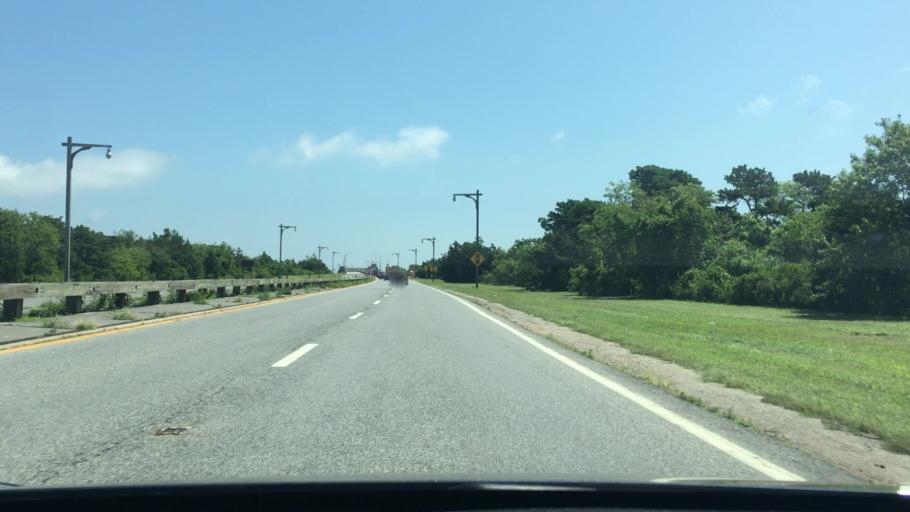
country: US
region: New York
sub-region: Nassau County
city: Point Lookout
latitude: 40.6035
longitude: -73.5761
